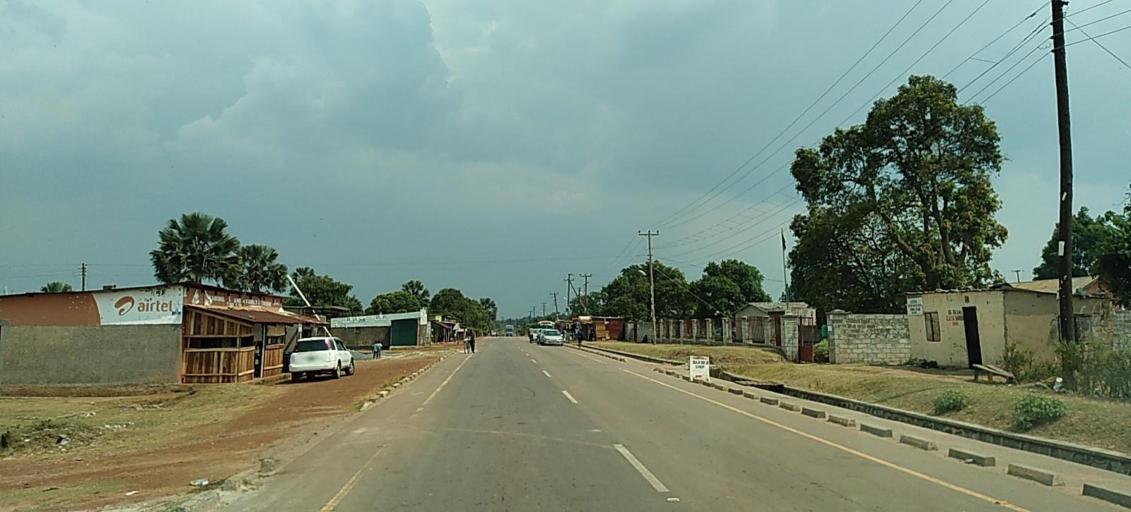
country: ZM
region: Copperbelt
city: Kalulushi
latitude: -12.8510
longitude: 28.1371
